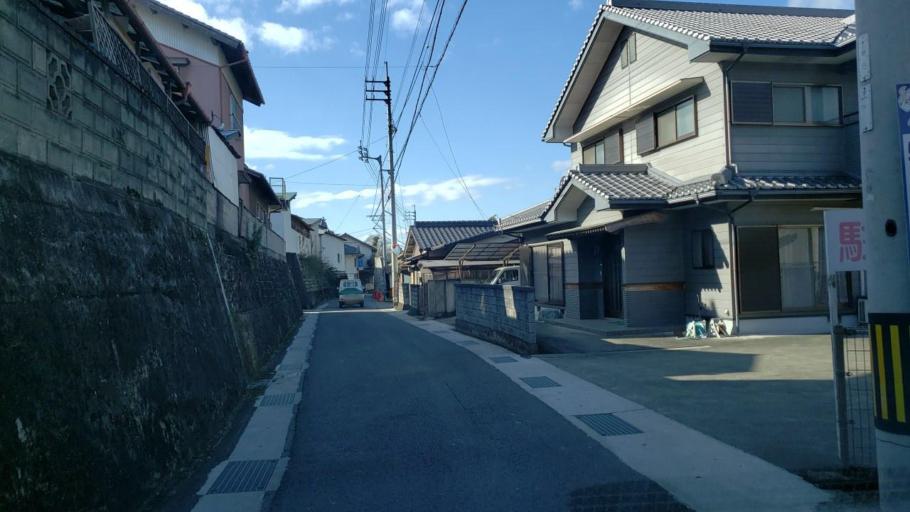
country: JP
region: Tokushima
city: Wakimachi
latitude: 34.0409
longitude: 134.0314
